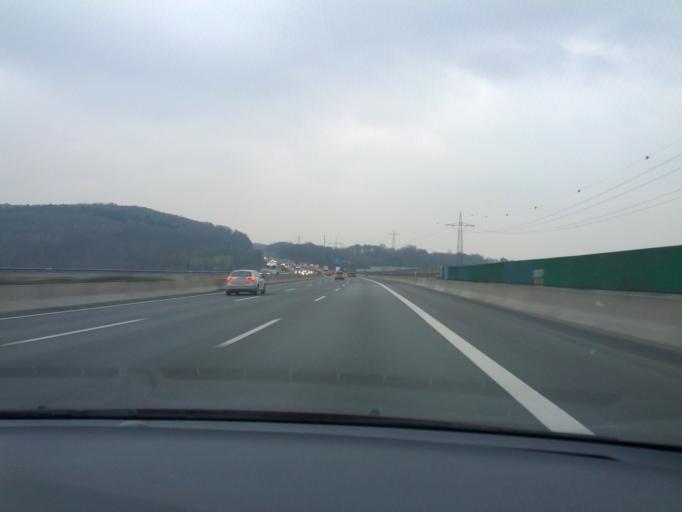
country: DE
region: North Rhine-Westphalia
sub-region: Regierungsbezirk Arnsberg
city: Hagen
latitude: 51.4131
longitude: 7.5043
